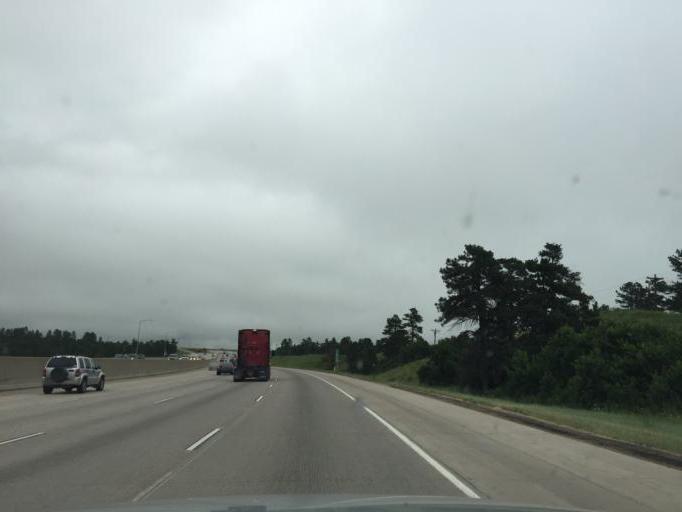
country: US
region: Colorado
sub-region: Douglas County
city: Castle Pines
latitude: 39.4419
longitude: -104.8756
